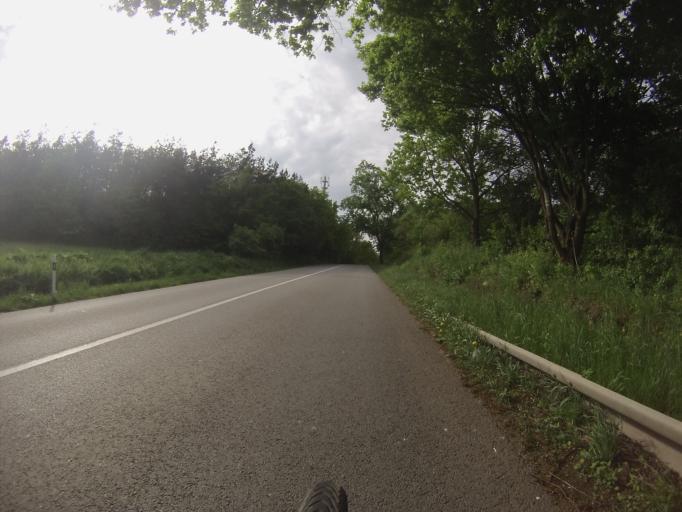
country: CZ
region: South Moravian
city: Veverska Bityska
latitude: 49.2561
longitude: 16.4496
